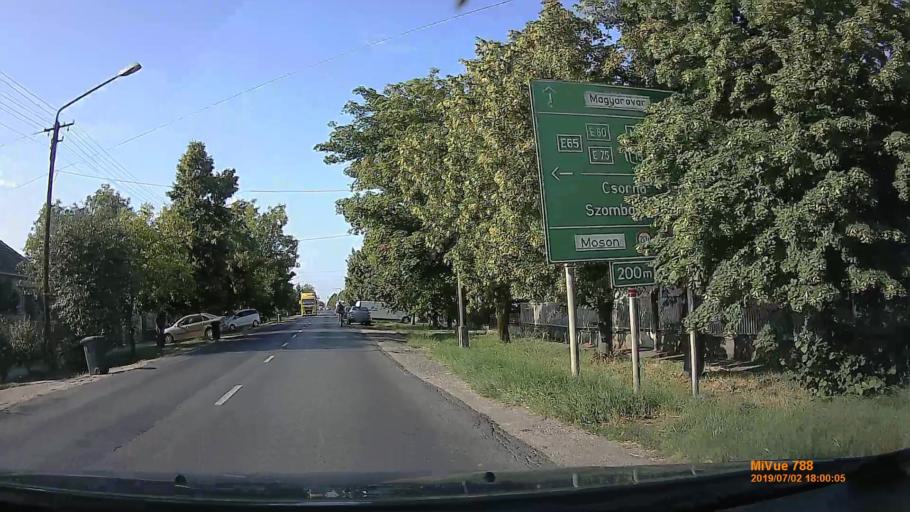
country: HU
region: Gyor-Moson-Sopron
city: Mosonmagyarovar
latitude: 47.8537
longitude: 17.2651
